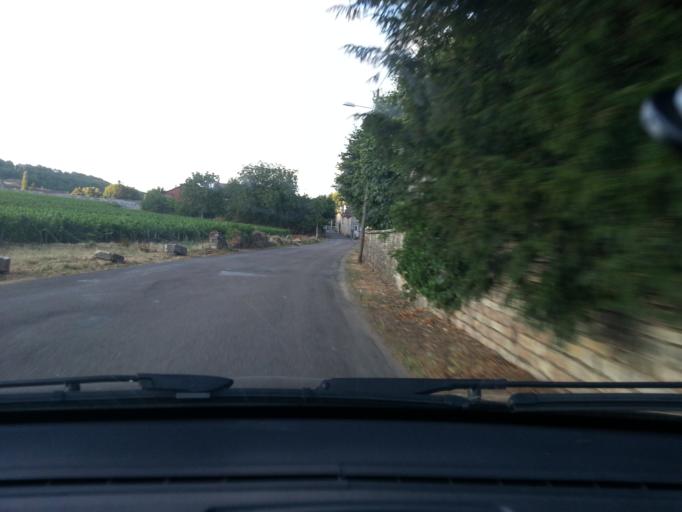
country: FR
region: Bourgogne
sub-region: Departement de Saone-et-Loire
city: Givry
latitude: 46.7715
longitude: 4.7217
